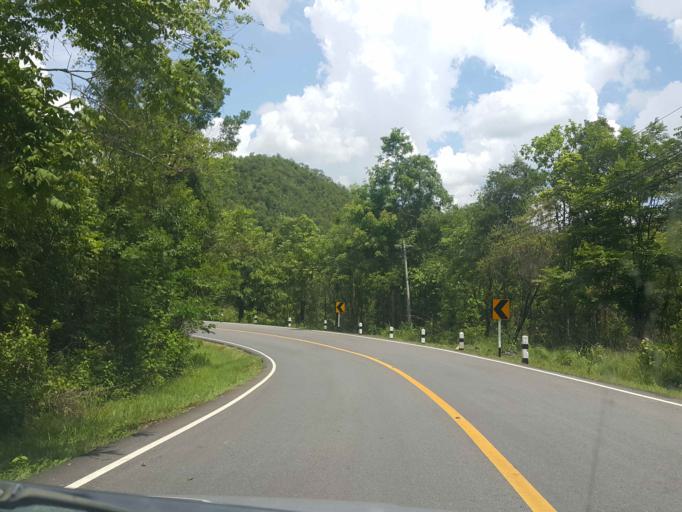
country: TH
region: Phayao
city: Chiang Muan
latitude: 18.8486
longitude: 100.3251
